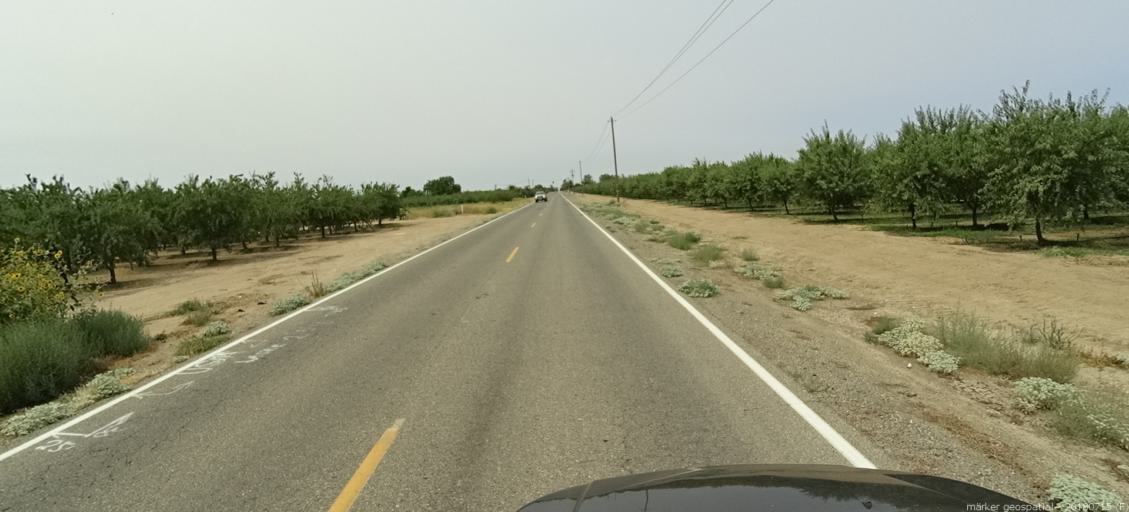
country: US
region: California
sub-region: Madera County
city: Madera Acres
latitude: 37.0212
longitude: -120.1106
